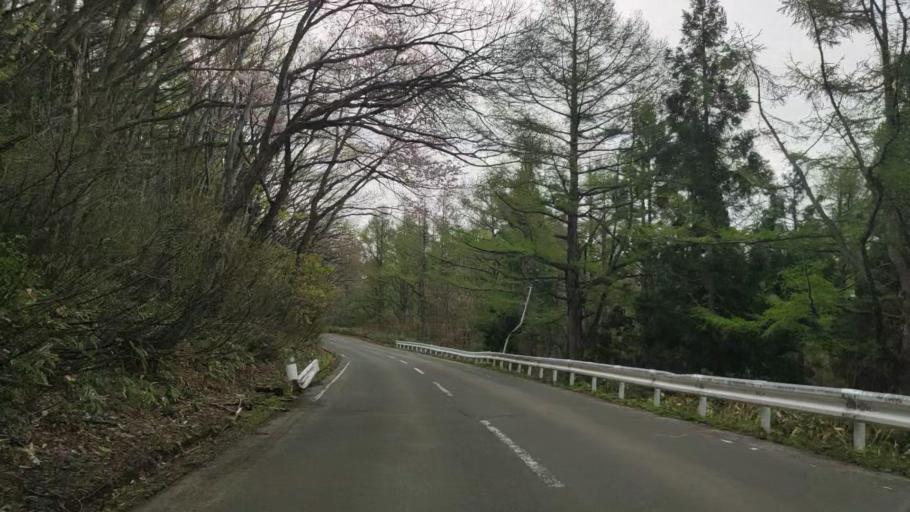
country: JP
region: Aomori
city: Aomori Shi
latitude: 40.7323
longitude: 140.8406
